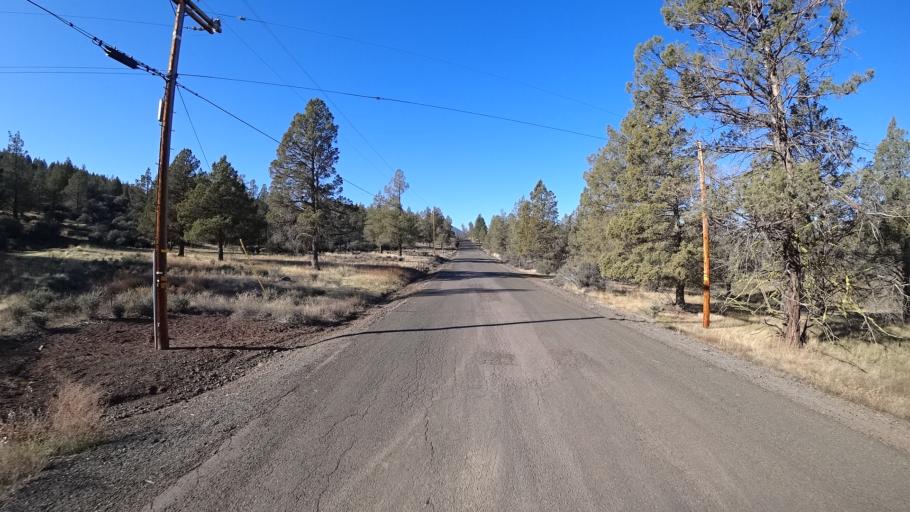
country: US
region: California
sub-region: Siskiyou County
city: Montague
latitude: 41.8899
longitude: -122.4377
